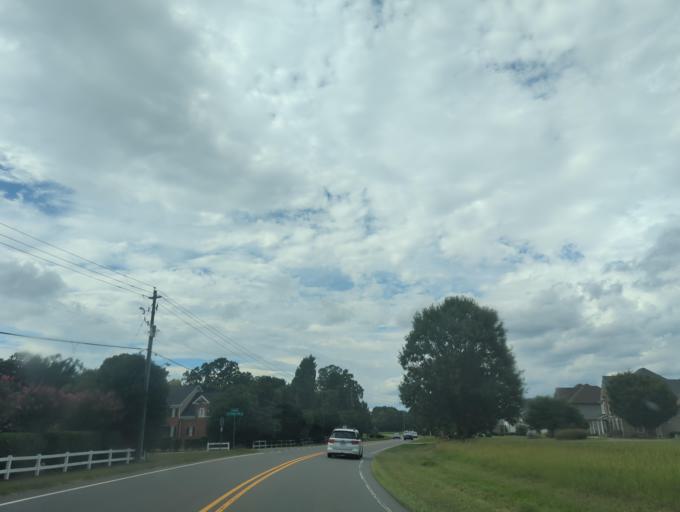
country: US
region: North Carolina
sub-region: Wake County
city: Fuquay-Varina
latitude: 35.6220
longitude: -78.7755
